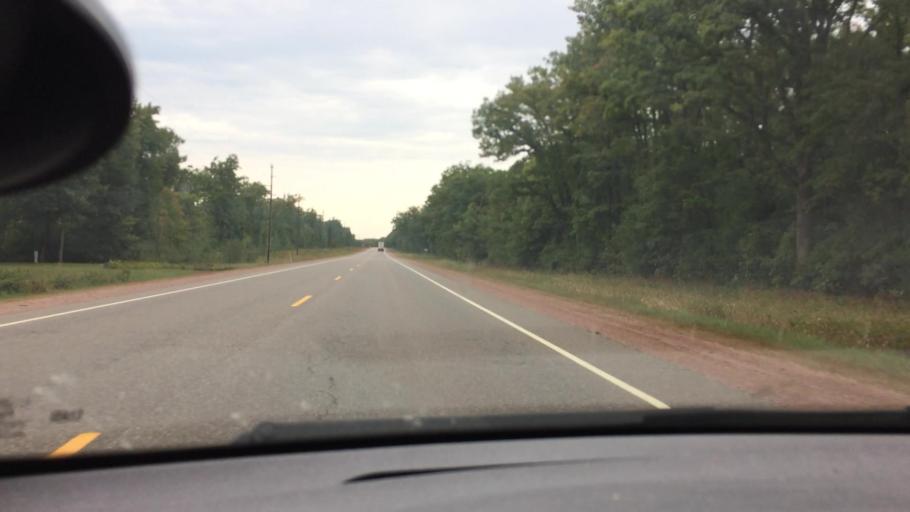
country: US
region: Wisconsin
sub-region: Clark County
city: Neillsville
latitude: 44.5762
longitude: -90.7348
